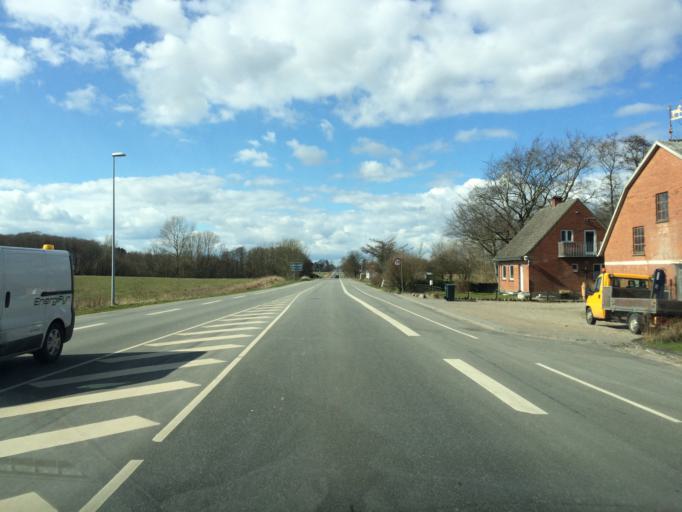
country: DK
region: South Denmark
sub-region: Assens Kommune
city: Arup
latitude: 55.4166
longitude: 10.0489
